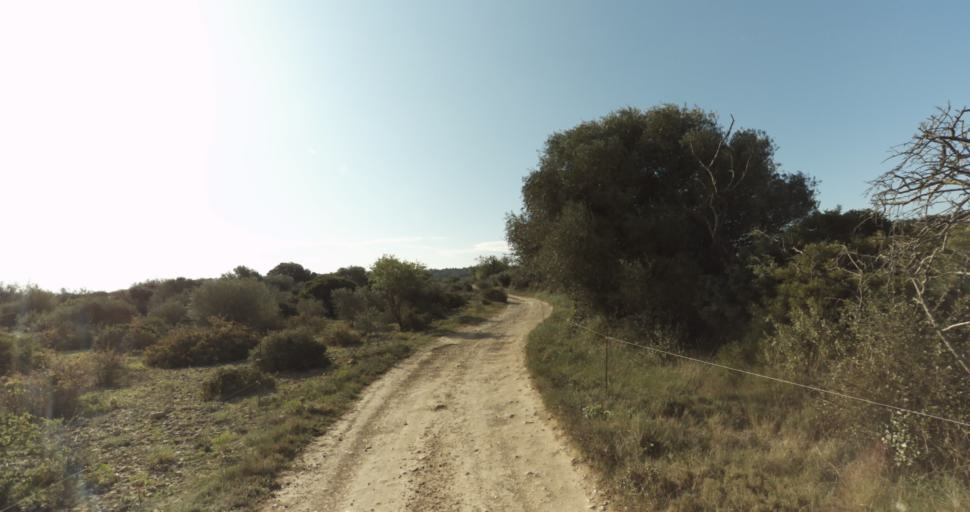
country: FR
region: Languedoc-Roussillon
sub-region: Departement de l'Aude
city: Leucate
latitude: 42.9401
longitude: 3.0106
